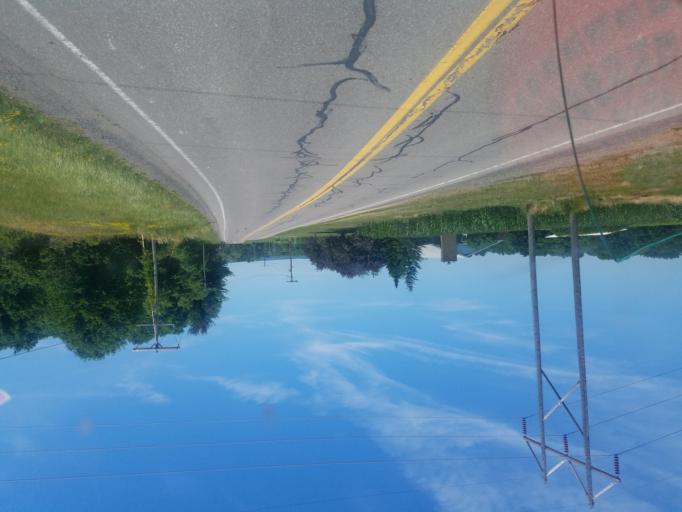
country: US
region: New York
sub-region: Yates County
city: Dundee
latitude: 42.5923
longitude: -76.9495
